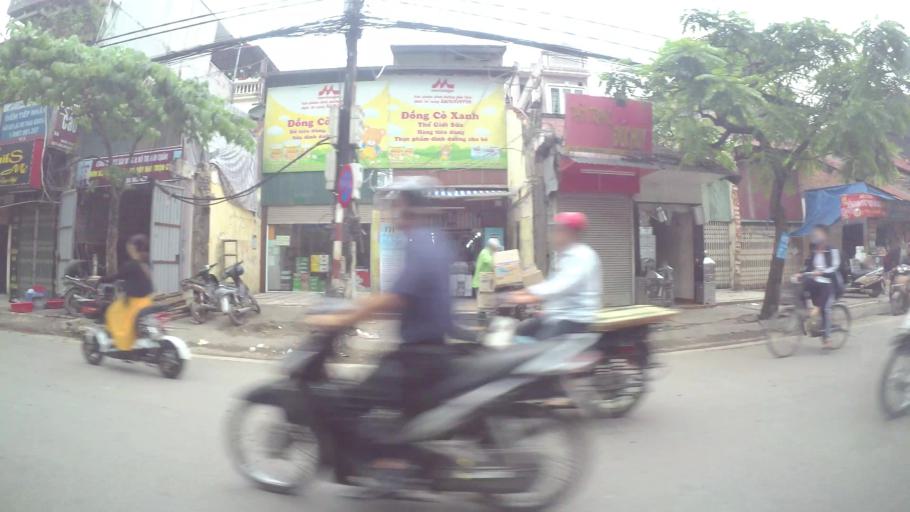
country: VN
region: Ha Noi
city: Hai BaTrung
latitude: 20.9955
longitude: 105.8505
